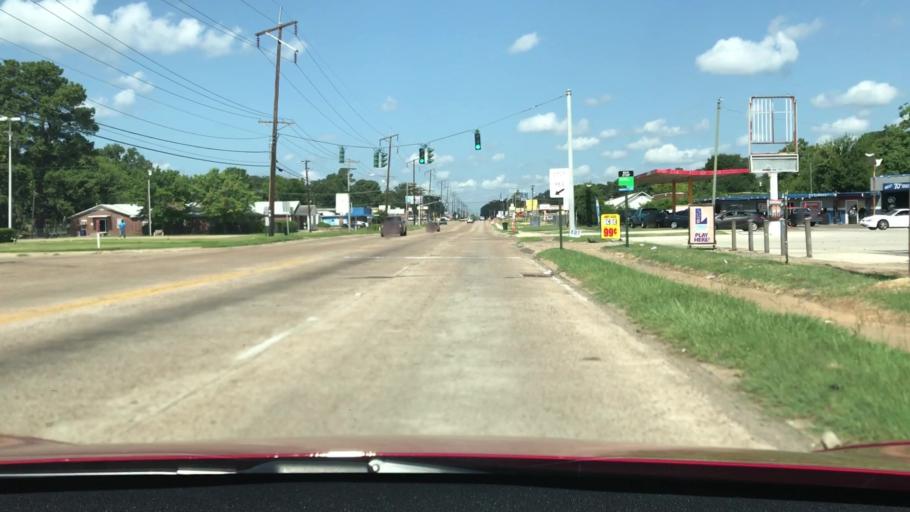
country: US
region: Louisiana
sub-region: Caddo Parish
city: Shreveport
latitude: 32.4420
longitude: -93.7851
